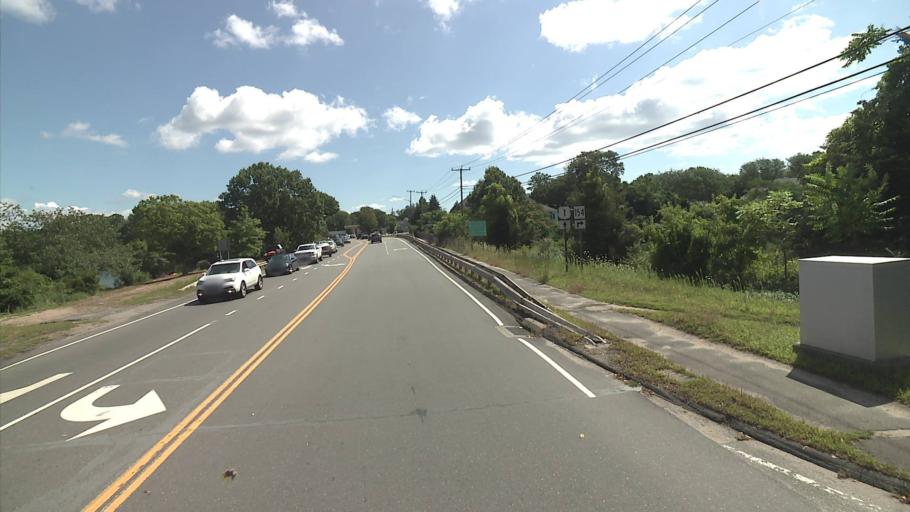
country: US
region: Connecticut
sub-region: Middlesex County
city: Saybrook Manor
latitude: 41.2876
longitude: -72.3931
